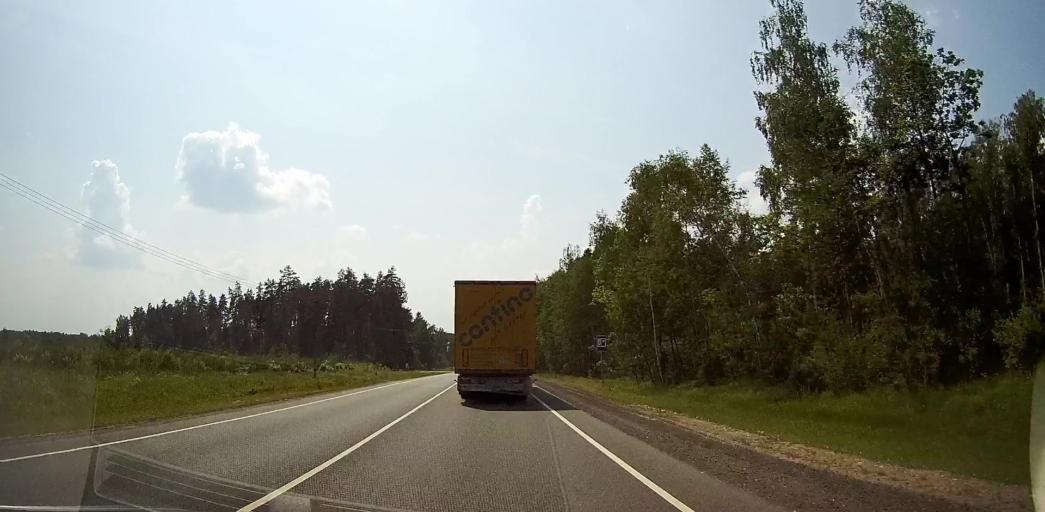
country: RU
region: Moskovskaya
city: Meshcherino
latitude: 55.2051
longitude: 38.3792
